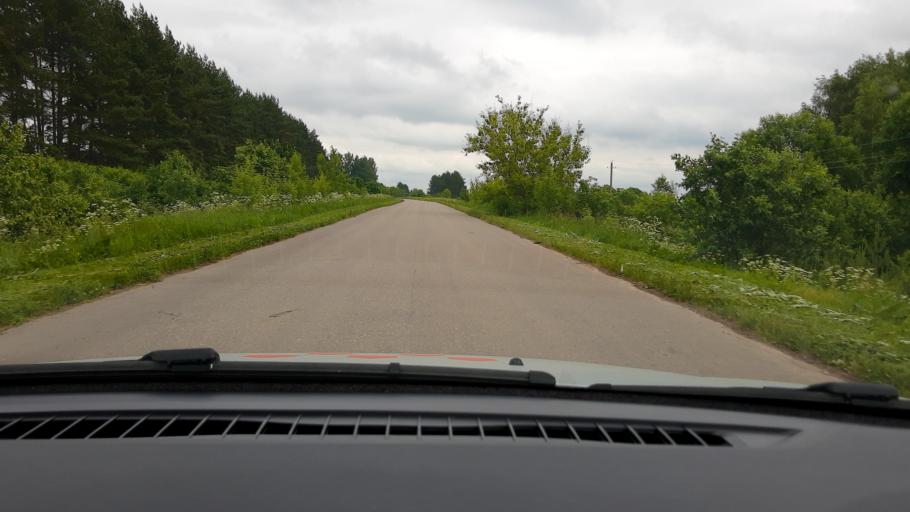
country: RU
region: Nizjnij Novgorod
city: Bogorodsk
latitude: 56.0628
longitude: 43.4985
